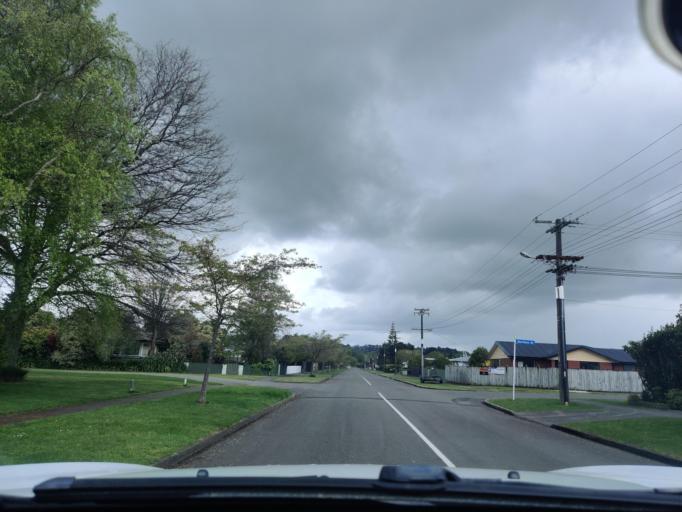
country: NZ
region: Manawatu-Wanganui
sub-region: Palmerston North City
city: Palmerston North
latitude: -40.2902
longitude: 175.7523
